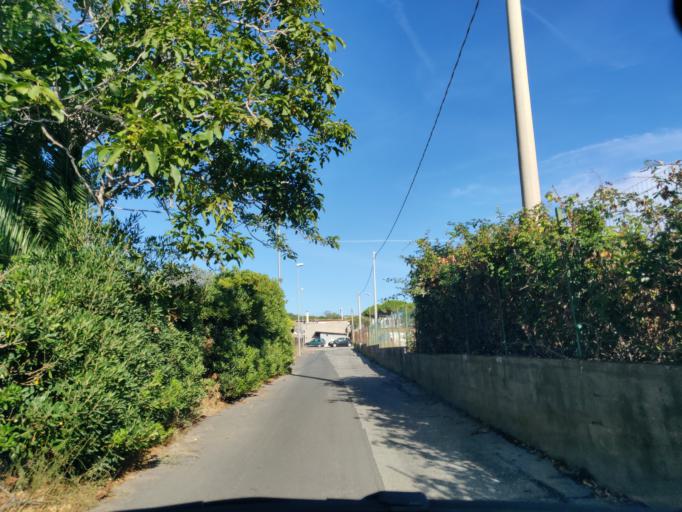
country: IT
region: Latium
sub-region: Citta metropolitana di Roma Capitale
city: Civitavecchia
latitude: 42.1041
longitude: 11.7952
